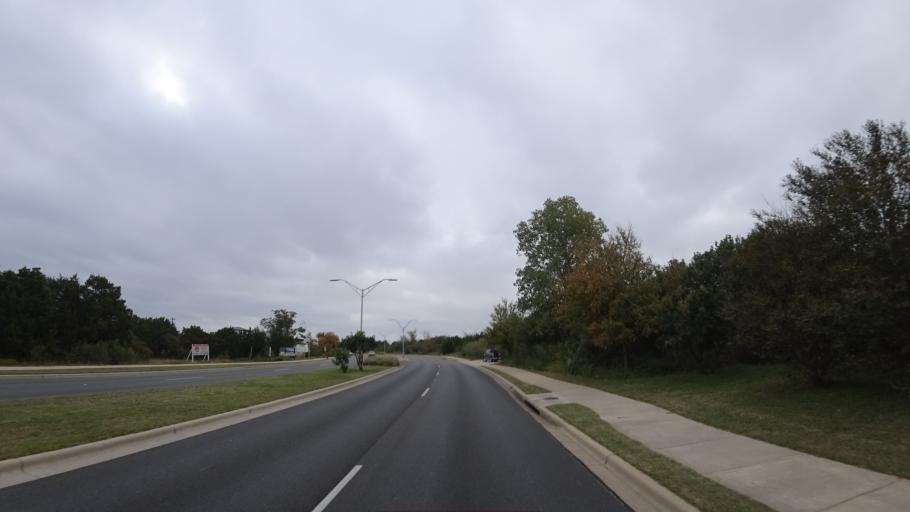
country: US
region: Texas
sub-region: Williamson County
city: Cedar Park
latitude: 30.5055
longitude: -97.8487
